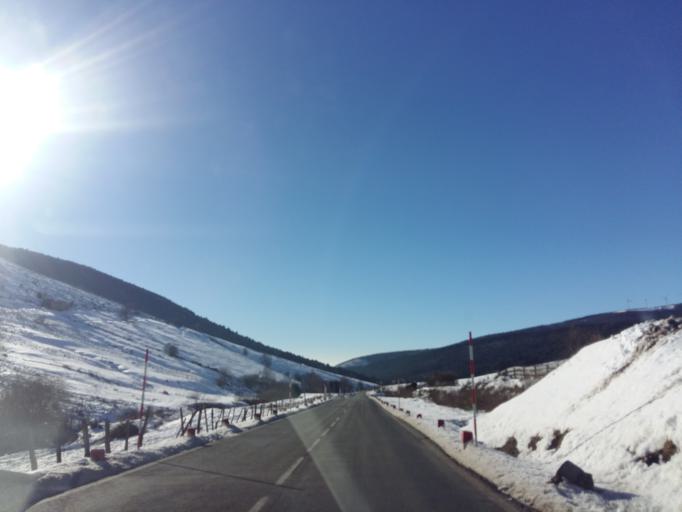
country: ES
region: Basque Country
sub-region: Bizkaia
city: Lanestosa
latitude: 43.1407
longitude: -3.4518
